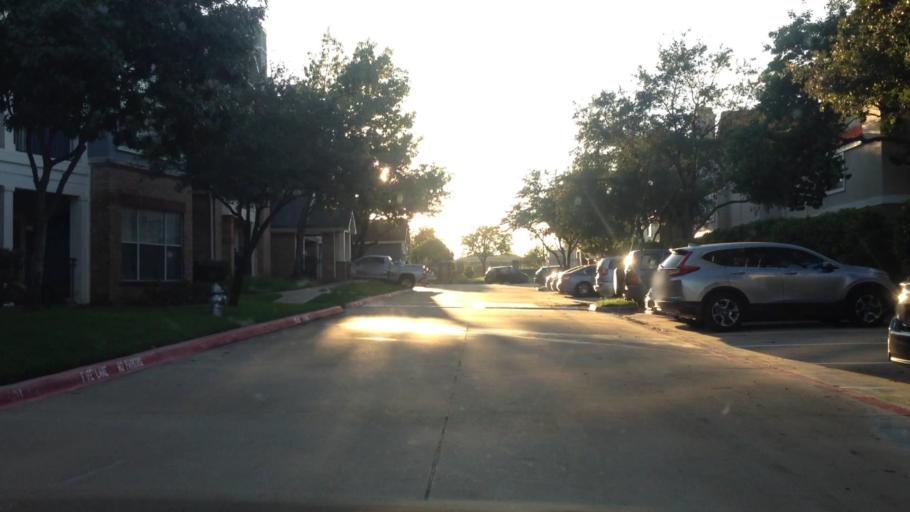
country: US
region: Texas
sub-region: Dallas County
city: Irving
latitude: 32.8836
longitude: -96.9619
